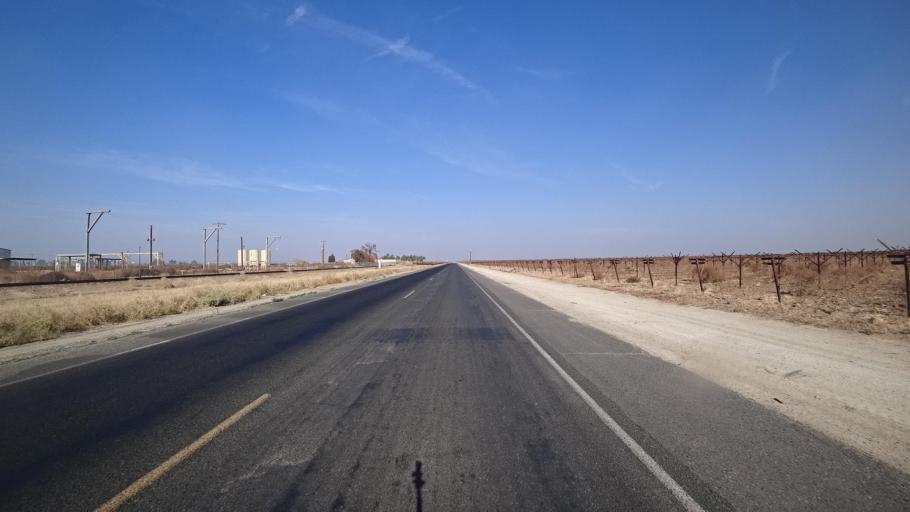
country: US
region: California
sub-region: Kern County
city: McFarland
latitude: 35.6764
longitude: -119.1853
